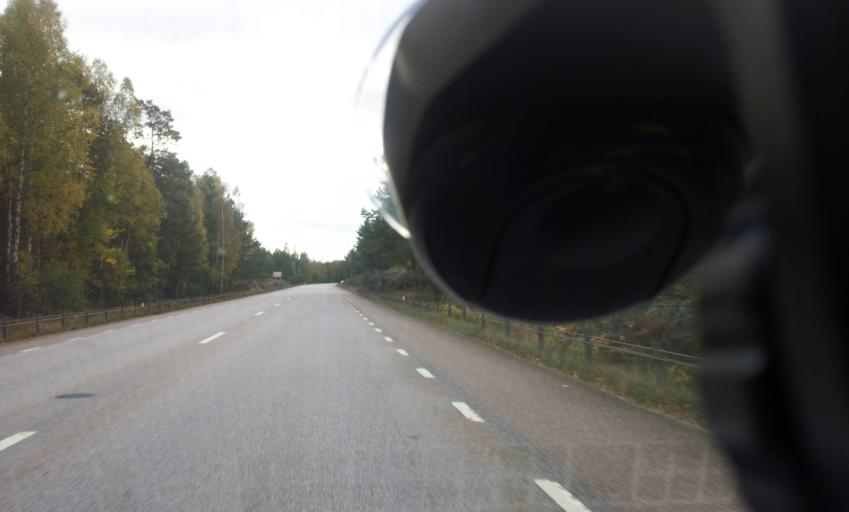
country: SE
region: Kalmar
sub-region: Oskarshamns Kommun
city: Oskarshamn
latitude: 57.5137
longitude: 16.5000
